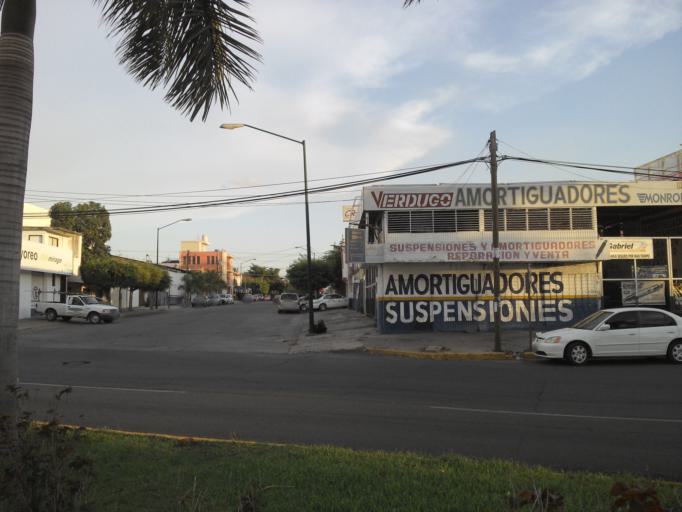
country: MX
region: Sinaloa
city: Culiacan
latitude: 24.8018
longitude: -107.3987
